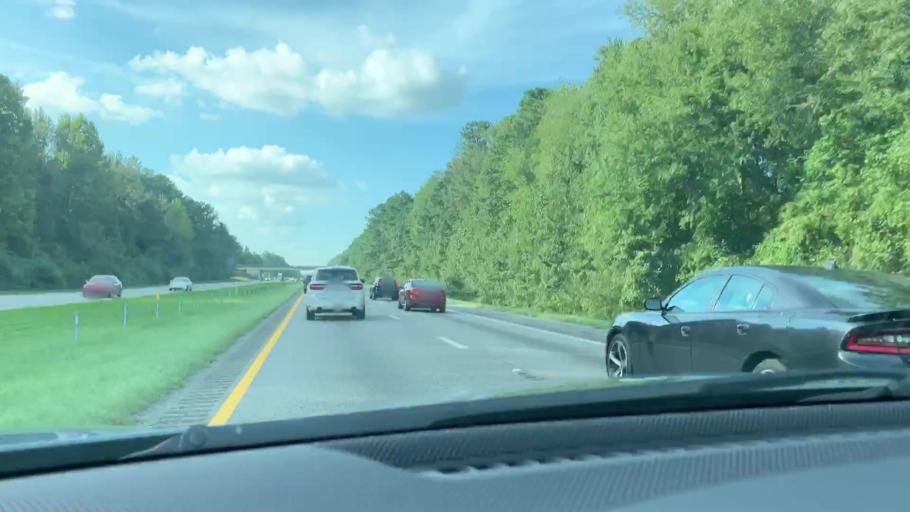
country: US
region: South Carolina
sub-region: Orangeburg County
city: Brookdale
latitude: 33.5315
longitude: -80.8016
